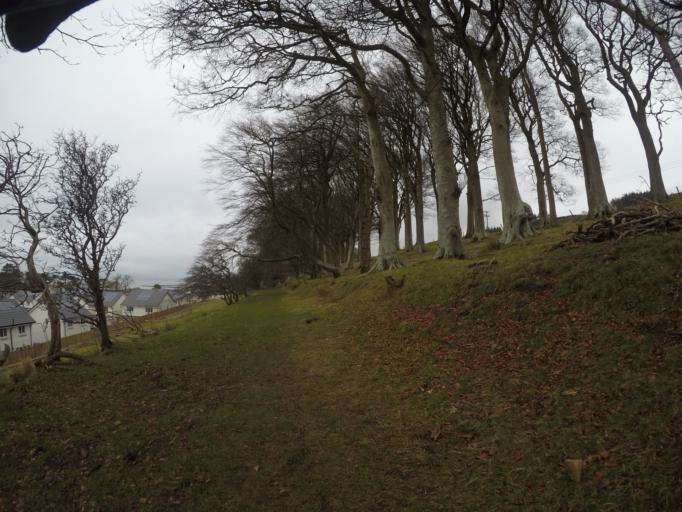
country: GB
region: Scotland
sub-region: North Ayrshire
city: Fairlie
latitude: 55.7585
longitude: -4.8496
